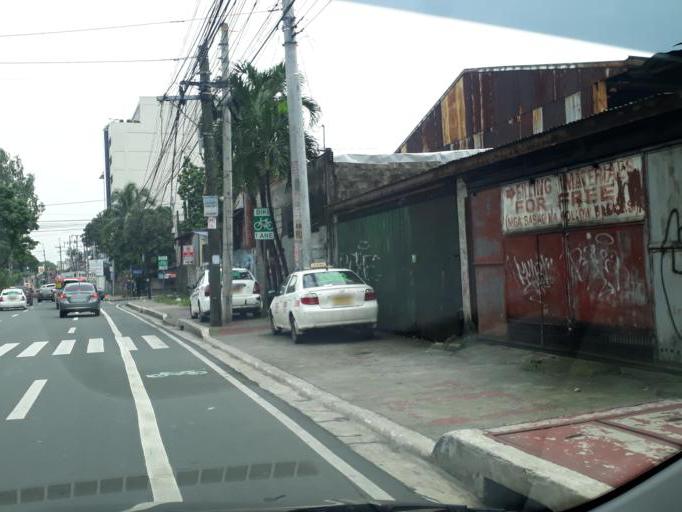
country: PH
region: Metro Manila
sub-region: Quezon City
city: Quezon City
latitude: 14.6386
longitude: 121.0550
